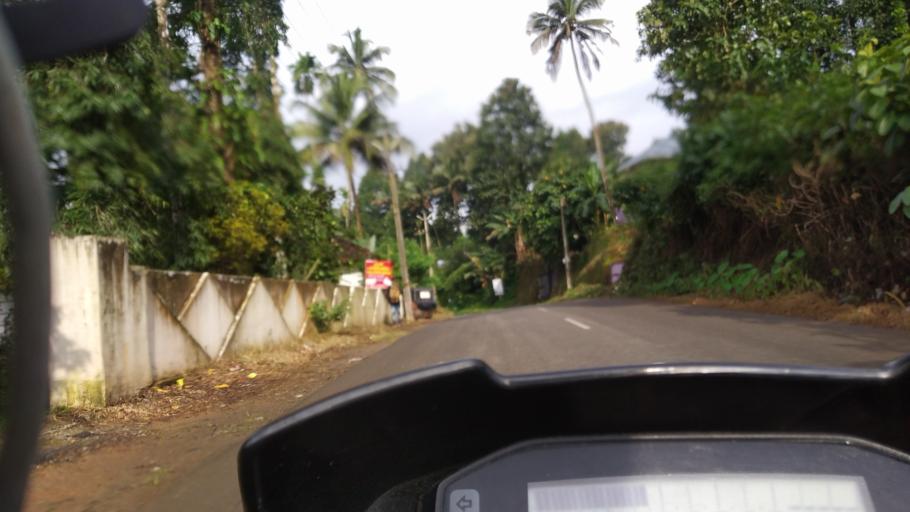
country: IN
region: Kerala
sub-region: Ernakulam
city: Kotamangalam
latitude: 10.0513
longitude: 76.7098
